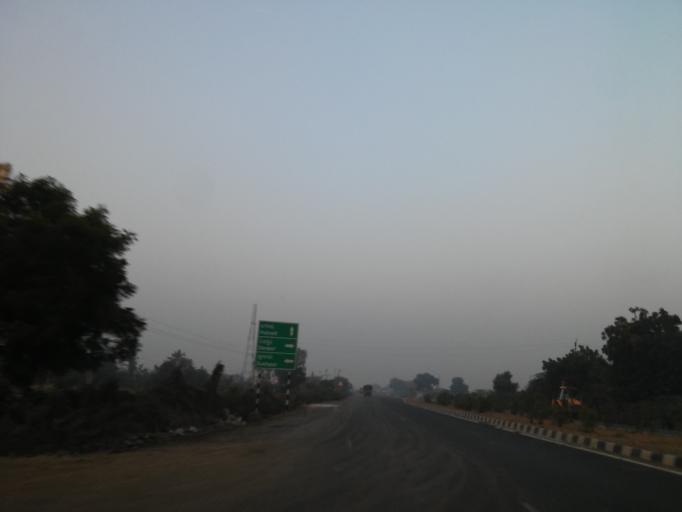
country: IN
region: Gujarat
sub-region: Surendranagar
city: Halvad
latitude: 23.0104
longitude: 71.2689
